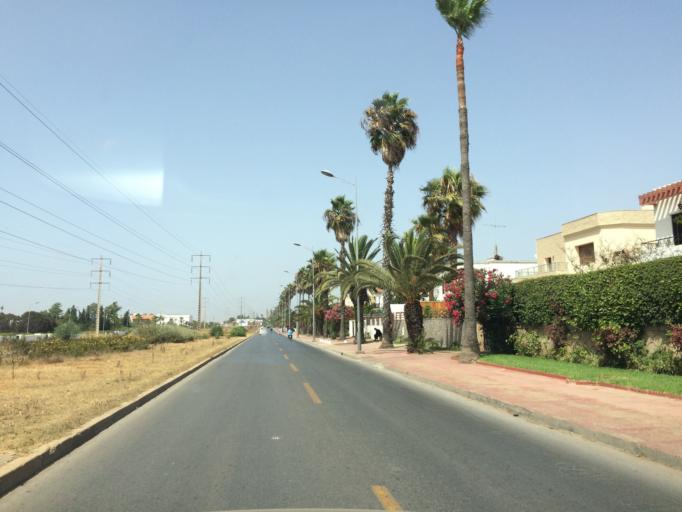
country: MA
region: Rabat-Sale-Zemmour-Zaer
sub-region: Skhirate-Temara
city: Temara
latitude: 33.9654
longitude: -6.8701
